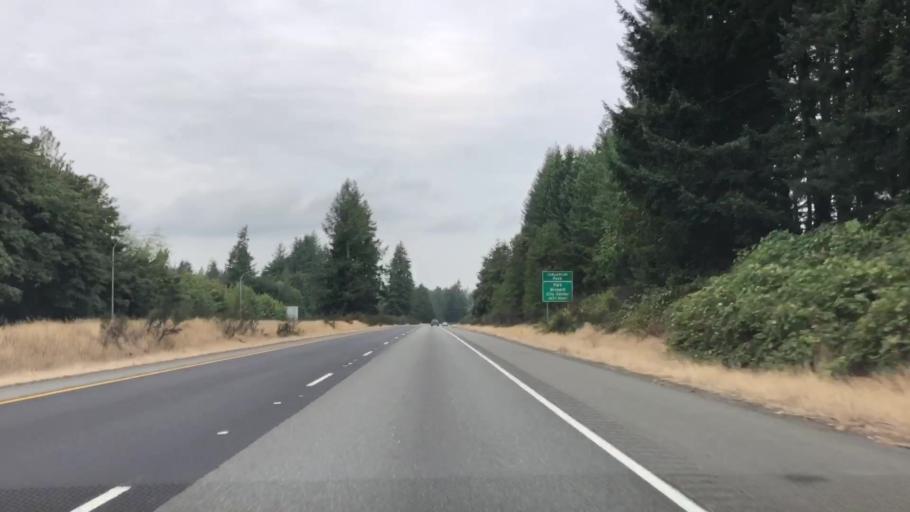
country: US
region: Washington
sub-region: Kitsap County
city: Bethel
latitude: 47.5146
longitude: -122.6553
